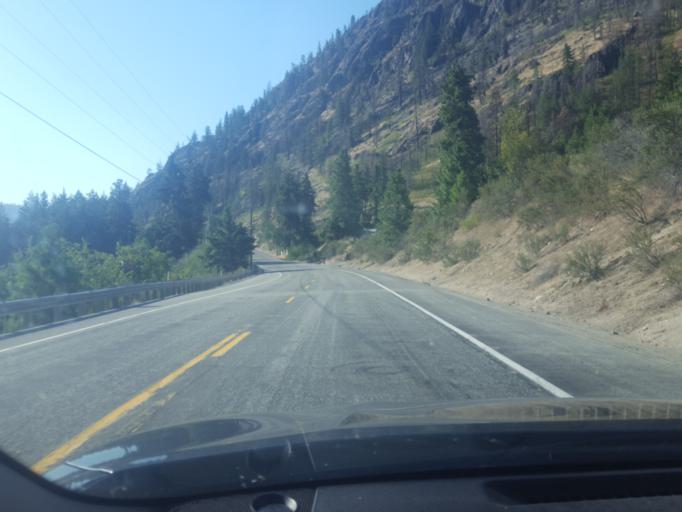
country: US
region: Washington
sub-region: Chelan County
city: Granite Falls
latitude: 47.9852
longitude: -120.2329
